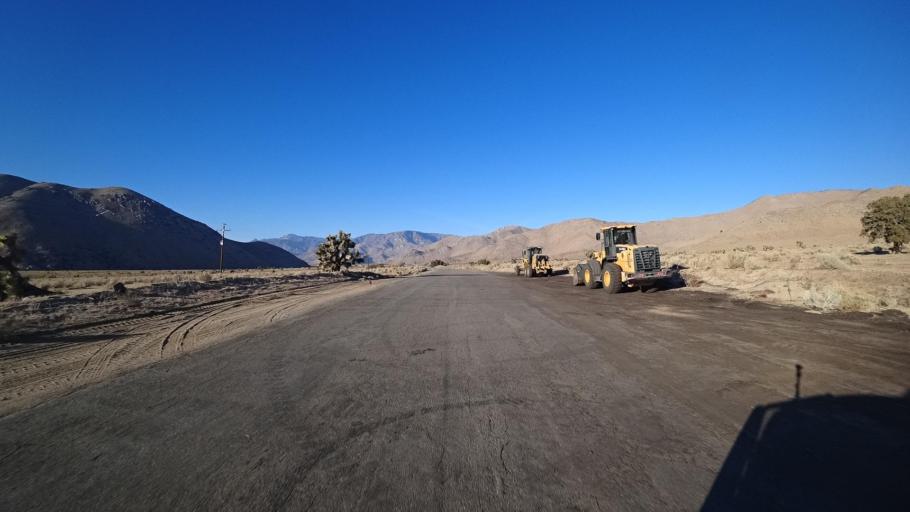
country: US
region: California
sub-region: Kern County
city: Weldon
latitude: 35.5950
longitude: -118.2404
